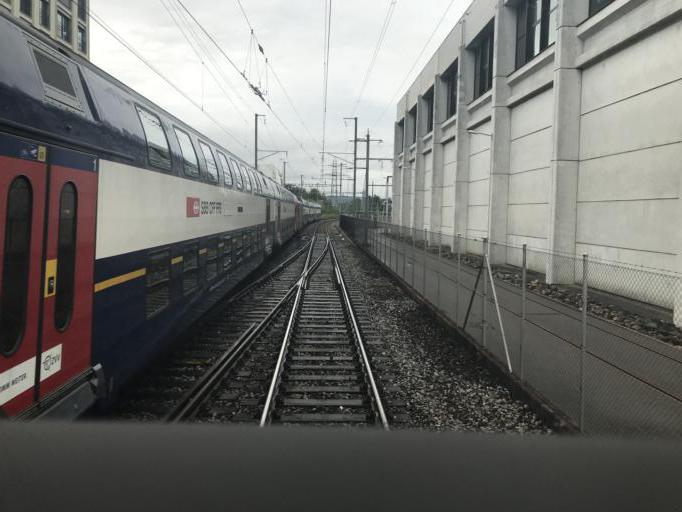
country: CH
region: Zurich
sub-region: Bezirk Zuerich
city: Zuerich (Kreis 11) / Seebach
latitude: 47.4233
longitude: 8.5552
